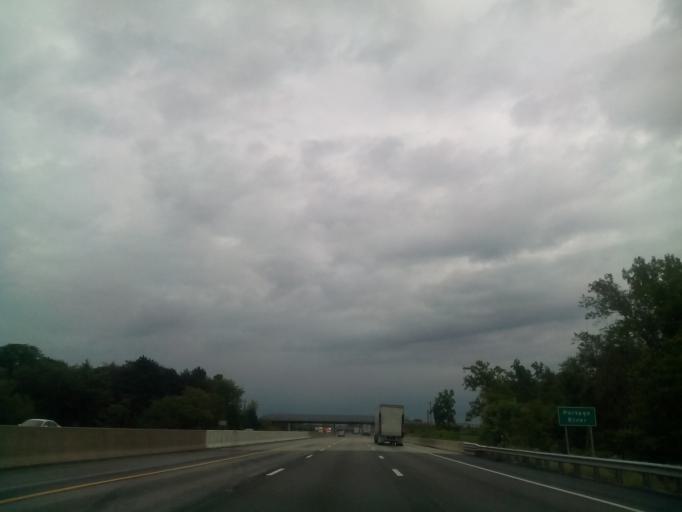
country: US
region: Ohio
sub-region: Ottawa County
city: Elmore
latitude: 41.4677
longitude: -83.3095
